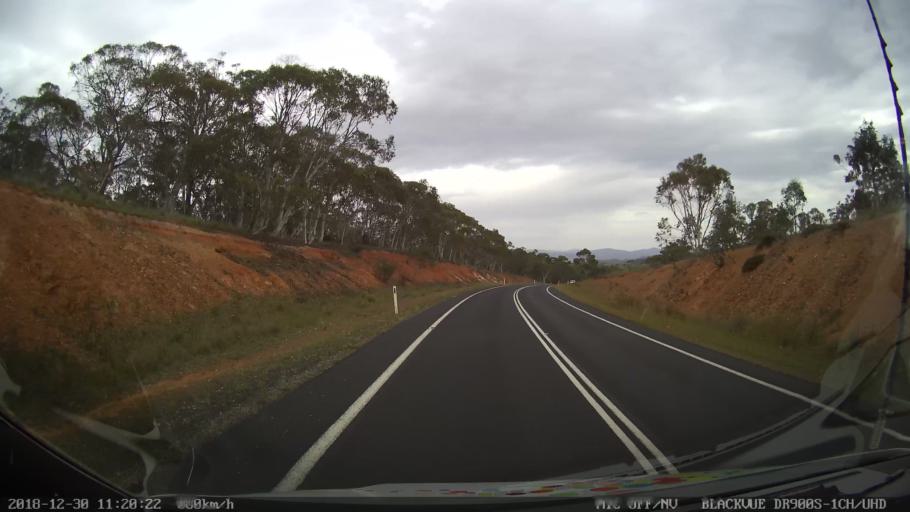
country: AU
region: New South Wales
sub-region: Snowy River
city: Jindabyne
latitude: -36.5190
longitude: 148.6895
